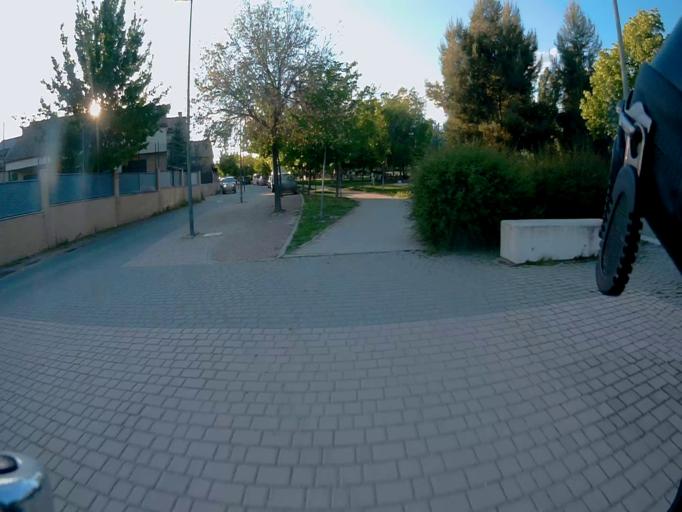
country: ES
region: Madrid
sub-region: Provincia de Madrid
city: Fuenlabrada
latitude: 40.3132
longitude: -3.7916
